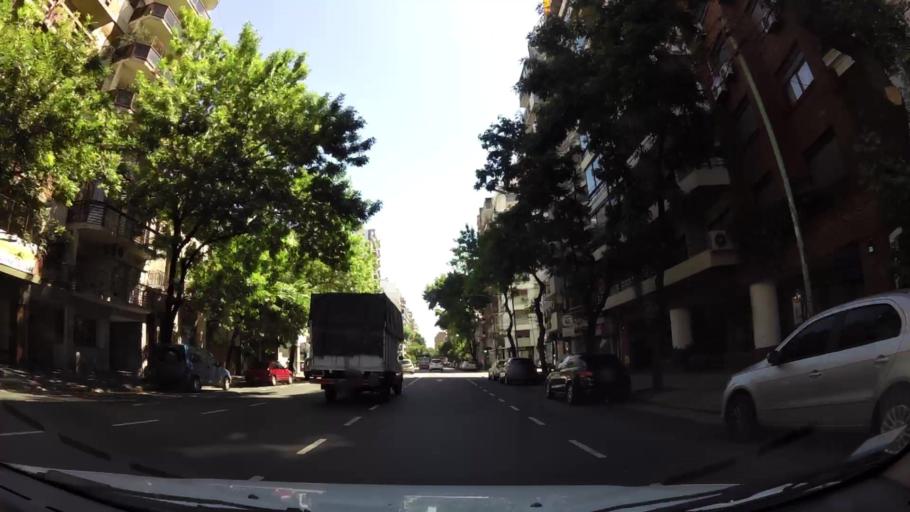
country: AR
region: Buenos Aires F.D.
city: Villa Santa Rita
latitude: -34.6258
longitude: -58.4486
